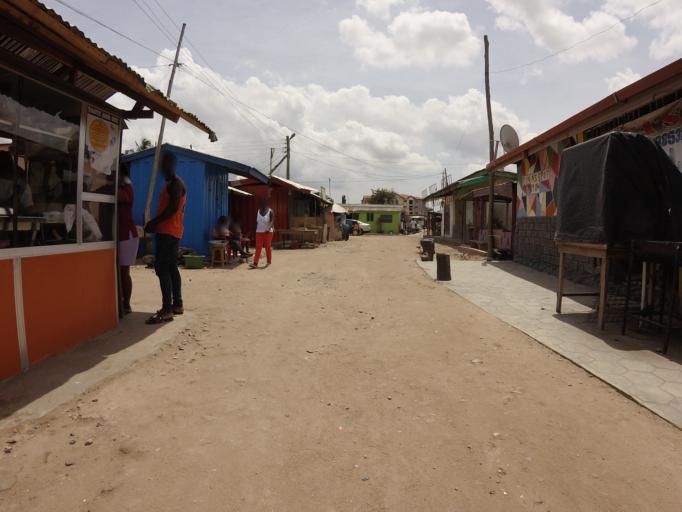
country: GH
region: Greater Accra
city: Dome
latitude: 5.6141
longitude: -0.2394
